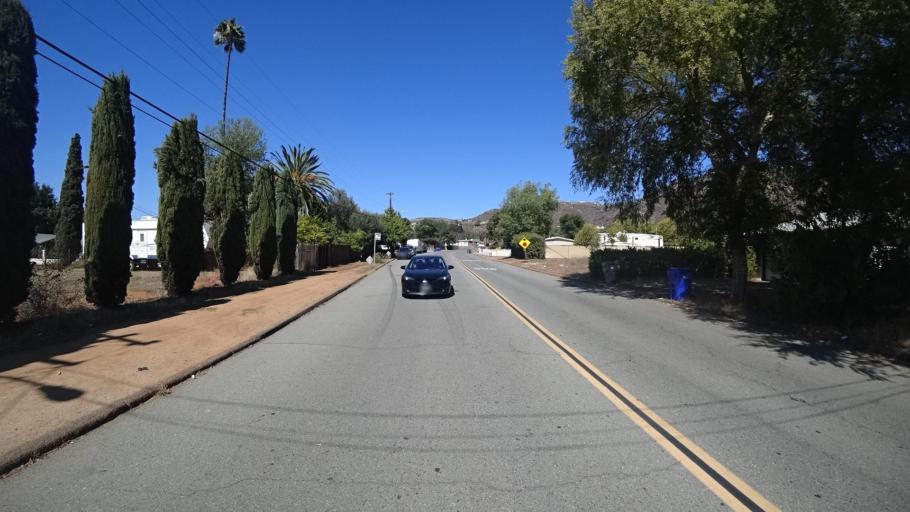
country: US
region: California
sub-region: San Diego County
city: Winter Gardens
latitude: 32.8221
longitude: -116.9498
